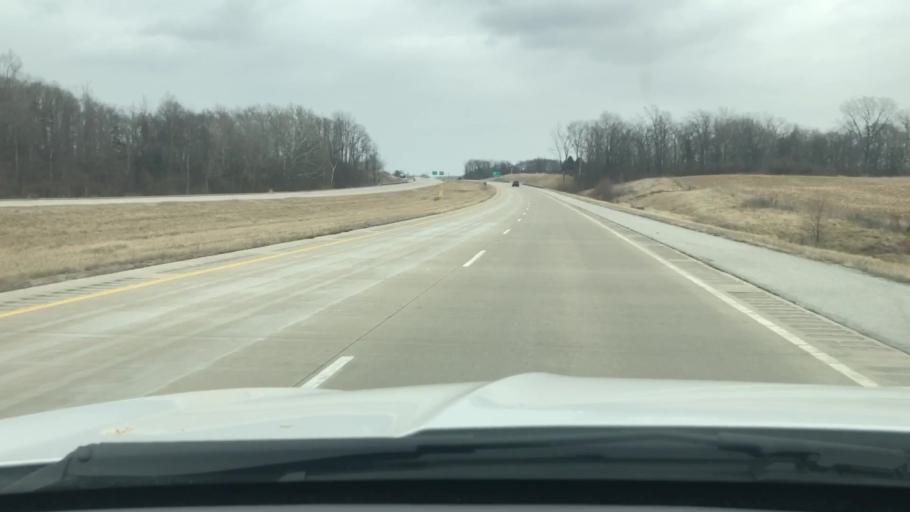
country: US
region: Indiana
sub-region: Cass County
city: Dunkirk
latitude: 40.7272
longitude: -86.4013
